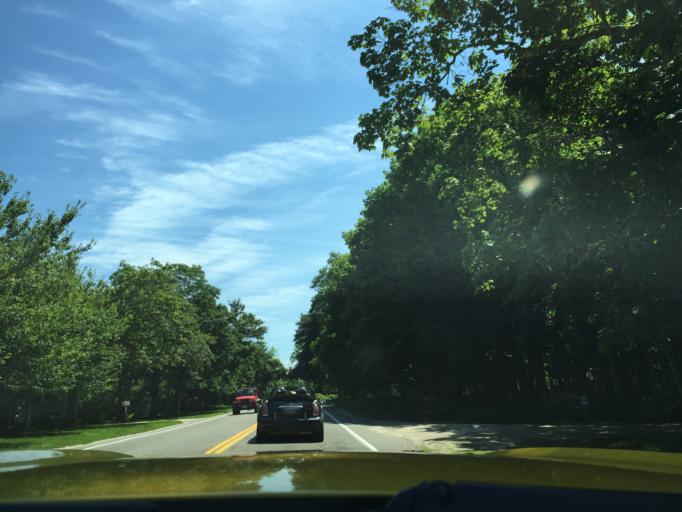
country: US
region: New York
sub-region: Suffolk County
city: Bridgehampton
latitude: 40.9301
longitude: -72.2901
